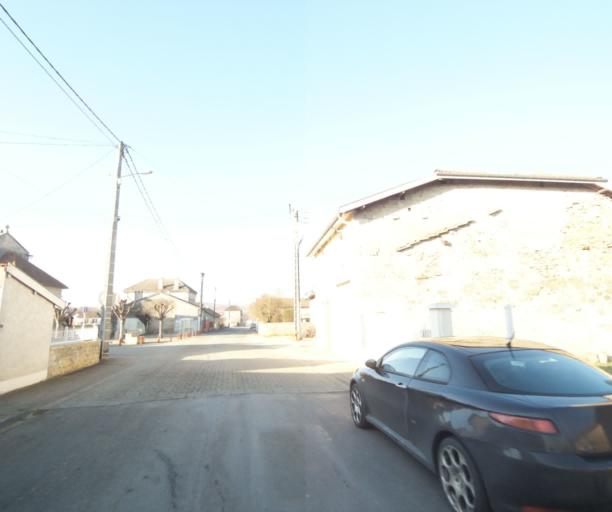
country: FR
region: Champagne-Ardenne
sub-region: Departement de la Haute-Marne
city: Chevillon
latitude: 48.5391
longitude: 5.1045
